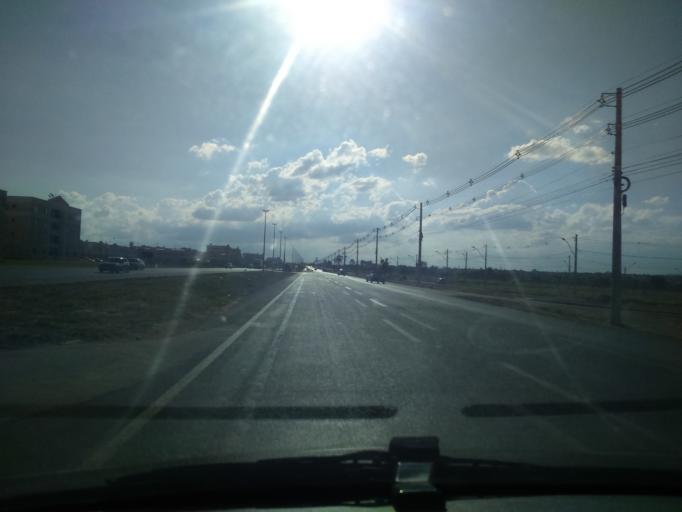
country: BR
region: Federal District
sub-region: Brasilia
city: Brasilia
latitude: -15.8885
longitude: -47.8055
